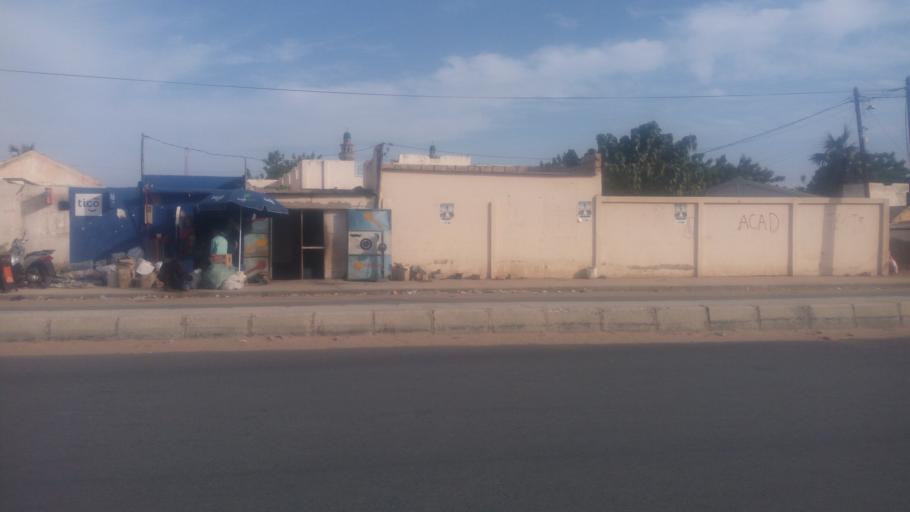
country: SN
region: Diourbel
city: Touba
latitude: 14.8507
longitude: -15.8820
